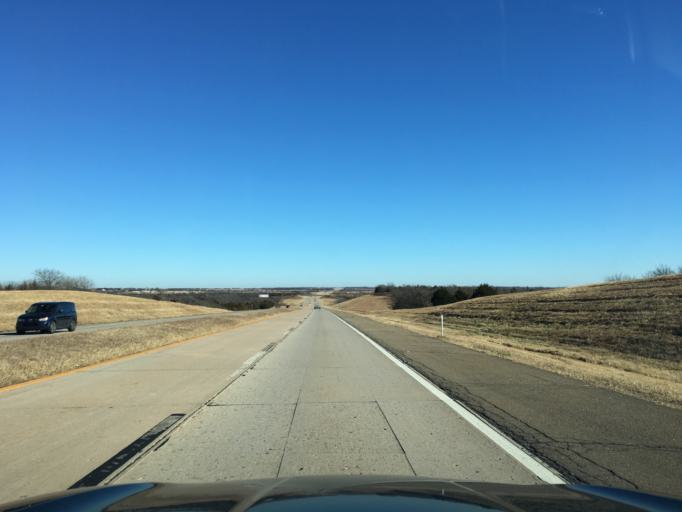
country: US
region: Oklahoma
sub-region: Payne County
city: Yale
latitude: 36.2241
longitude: -96.7264
